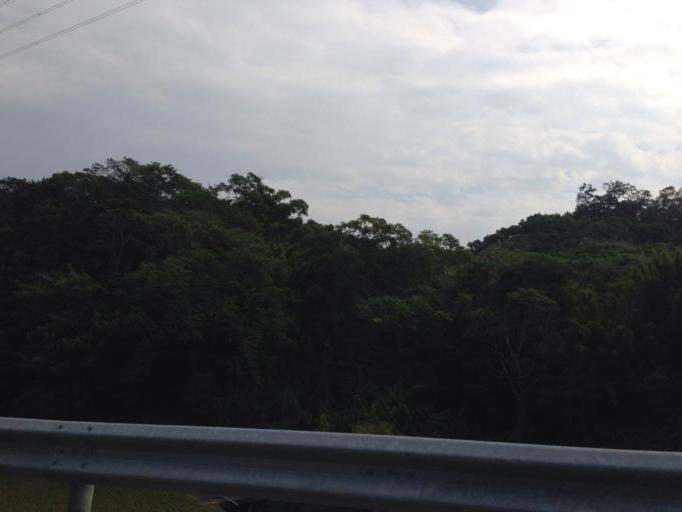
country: TW
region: Taiwan
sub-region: Hsinchu
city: Hsinchu
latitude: 24.7506
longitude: 120.9687
